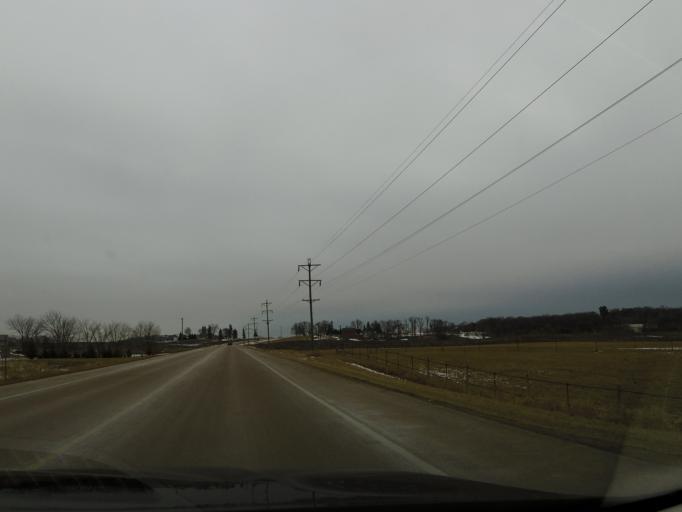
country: US
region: Minnesota
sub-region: Carver County
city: Watertown
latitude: 44.9499
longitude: -93.8370
